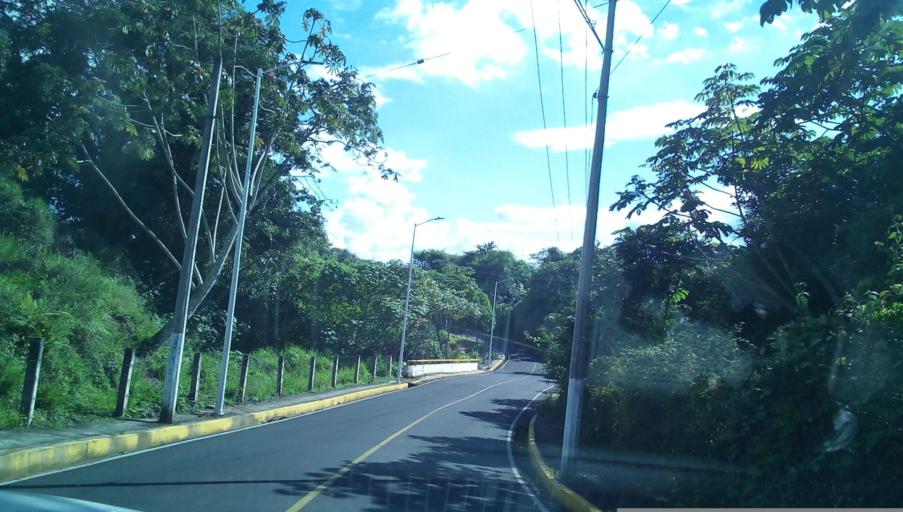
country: MX
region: Veracruz
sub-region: Cordoba
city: El Porvenir
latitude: 18.9042
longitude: -96.9227
